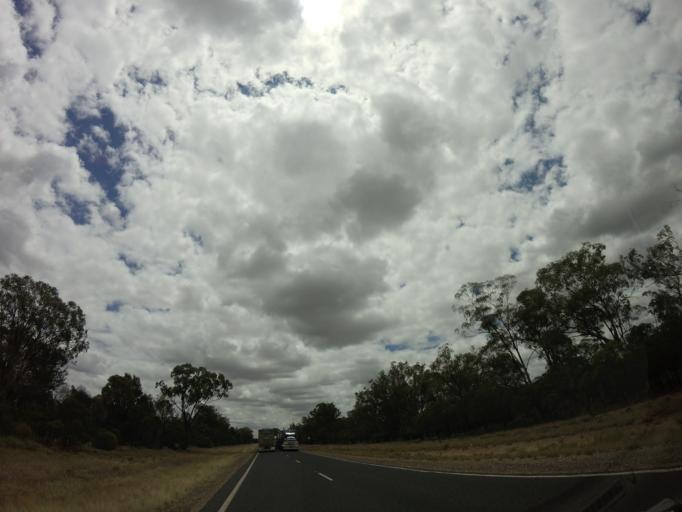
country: AU
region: Queensland
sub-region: Goondiwindi
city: Goondiwindi
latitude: -28.4338
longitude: 150.3016
